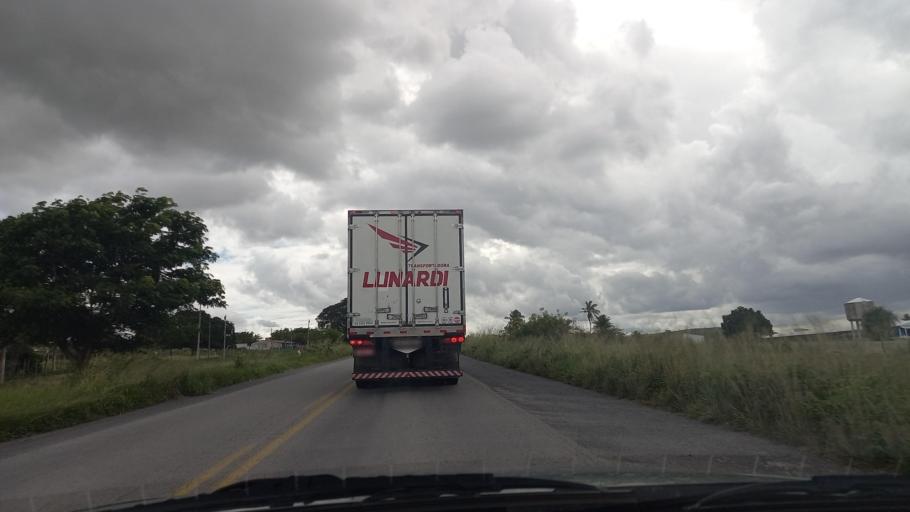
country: BR
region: Pernambuco
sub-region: Lajedo
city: Lajedo
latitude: -8.6659
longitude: -36.3637
